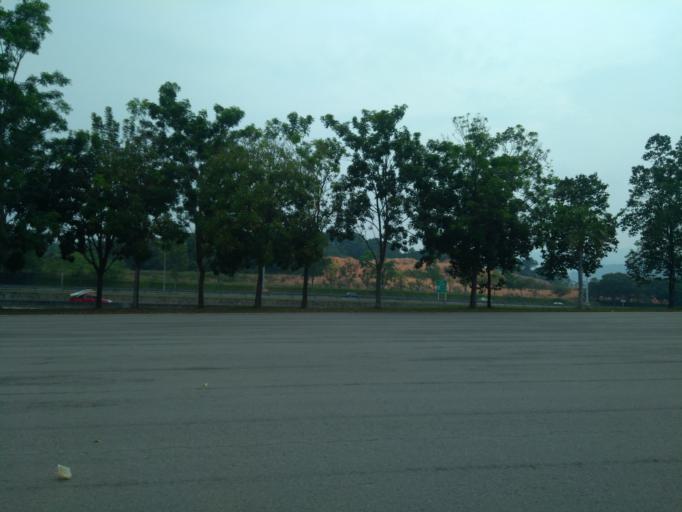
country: MY
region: Perak
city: Ipoh
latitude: 4.6631
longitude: 101.0810
